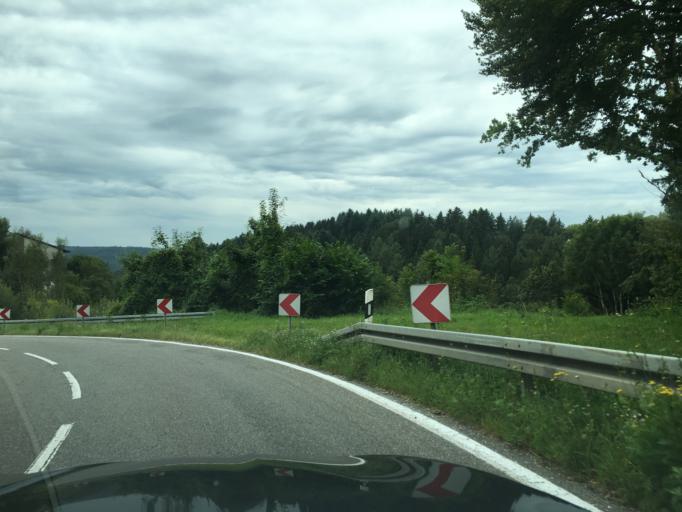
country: DE
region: Baden-Wuerttemberg
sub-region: Tuebingen Region
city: Rot
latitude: 47.8690
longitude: 9.1089
